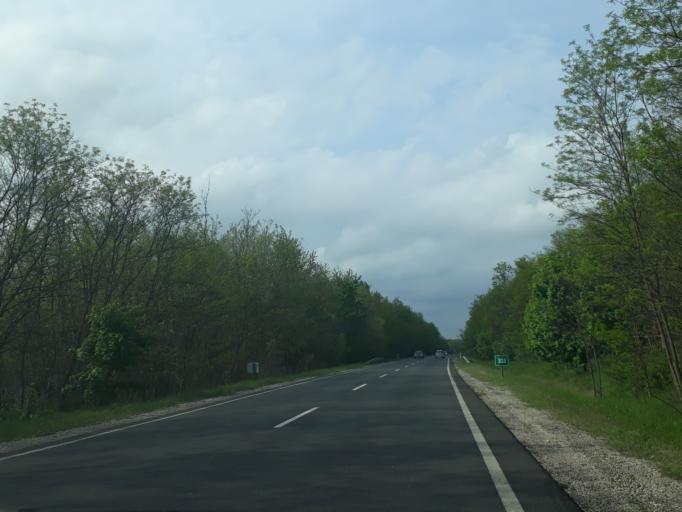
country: HU
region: Szabolcs-Szatmar-Bereg
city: Nyirtass
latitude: 48.1003
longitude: 21.9874
